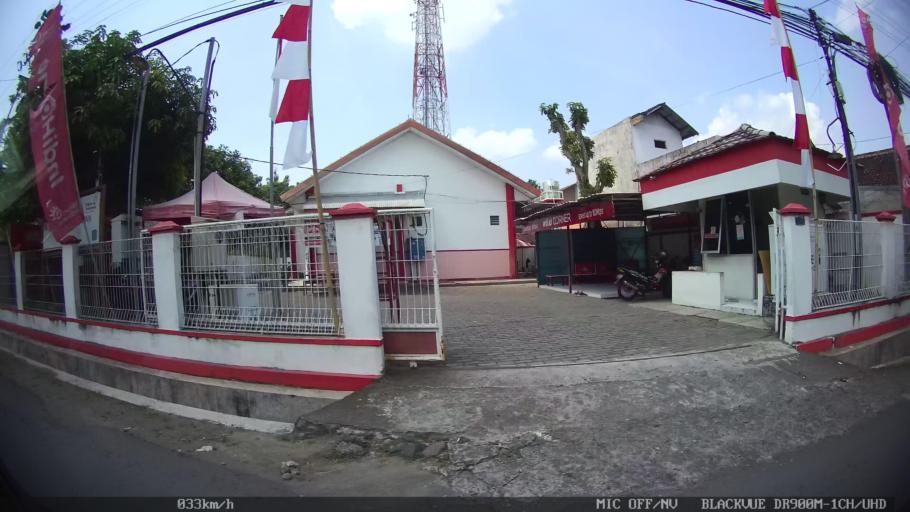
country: ID
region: Daerah Istimewa Yogyakarta
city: Yogyakarta
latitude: -7.8176
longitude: 110.4079
